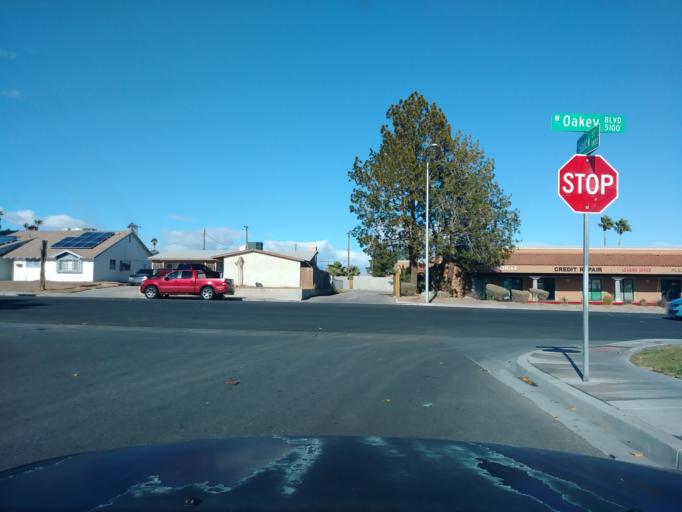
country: US
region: Nevada
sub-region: Clark County
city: Spring Valley
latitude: 36.1515
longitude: -115.2103
